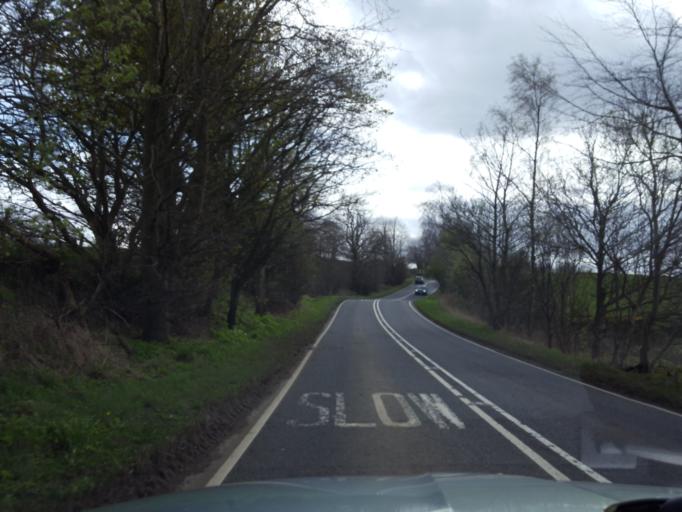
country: GB
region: Scotland
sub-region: West Lothian
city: Bathgate
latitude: 55.9555
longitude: -3.6585
